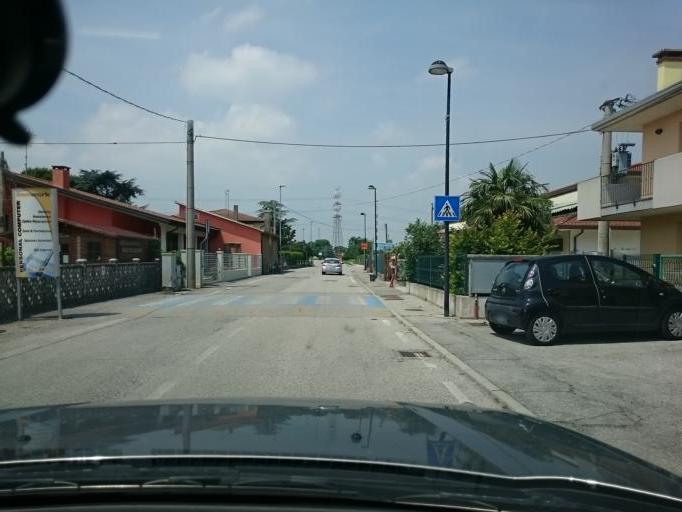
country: IT
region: Veneto
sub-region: Provincia di Padova
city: Codevigo
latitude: 45.2453
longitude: 12.1337
